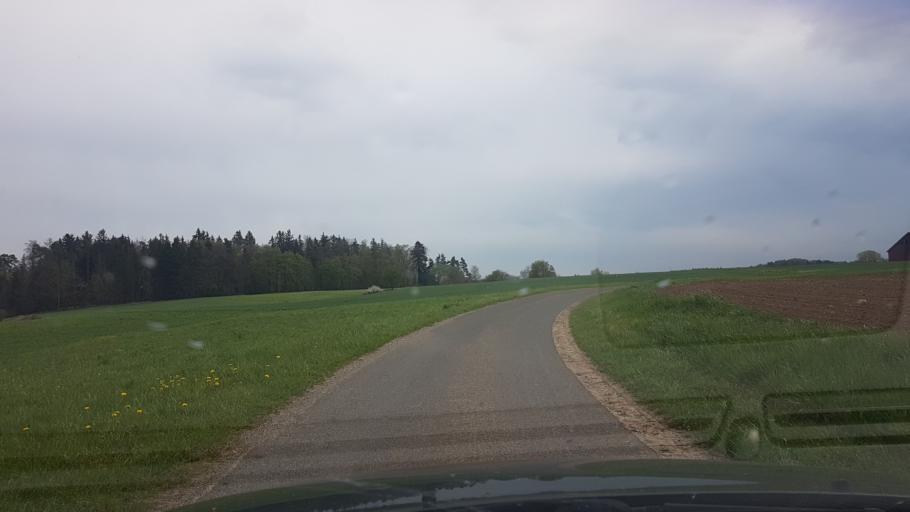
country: DE
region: Bavaria
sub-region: Upper Franconia
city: Wattendorf
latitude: 50.0114
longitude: 11.1534
